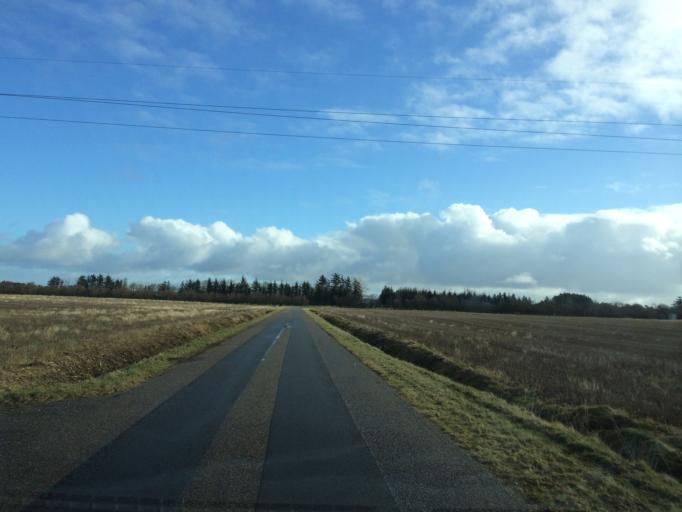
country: DK
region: Central Jutland
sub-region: Holstebro Kommune
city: Ulfborg
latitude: 56.2800
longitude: 8.3437
